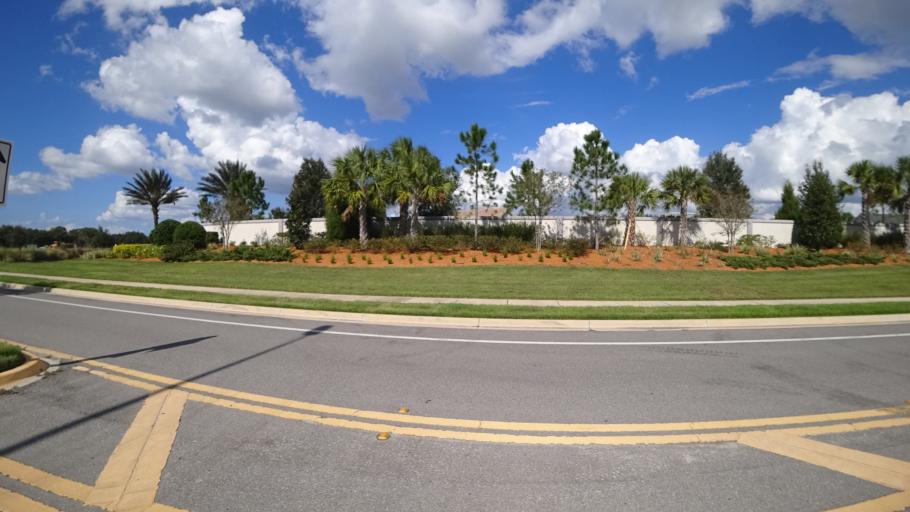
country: US
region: Florida
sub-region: Manatee County
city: Ellenton
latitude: 27.4675
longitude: -82.4287
